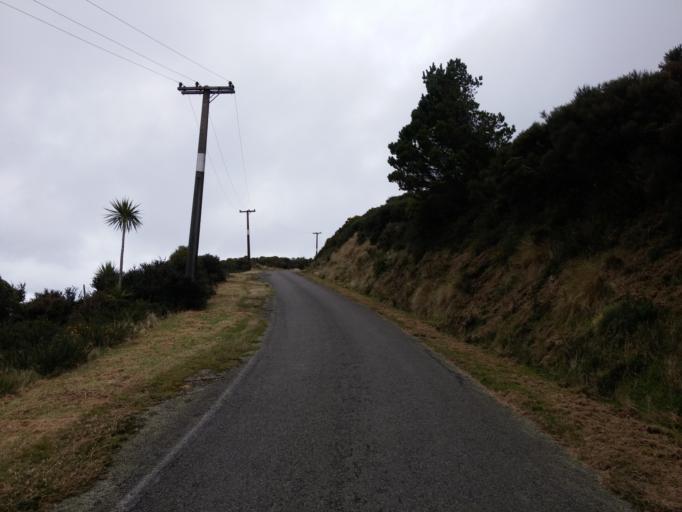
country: NZ
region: Wellington
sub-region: Wellington City
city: Brooklyn
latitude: -41.3218
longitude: 174.7318
